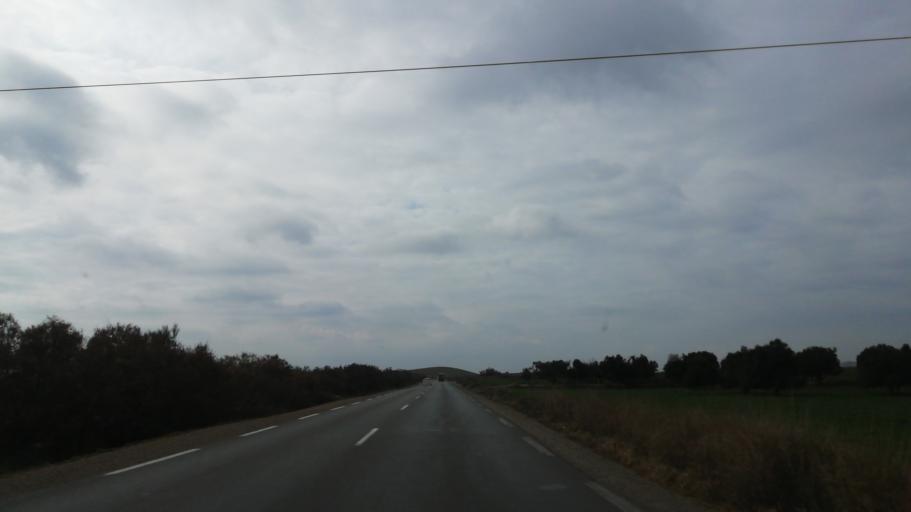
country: DZ
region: Oran
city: Sidi ech Chahmi
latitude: 35.5984
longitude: -0.4452
